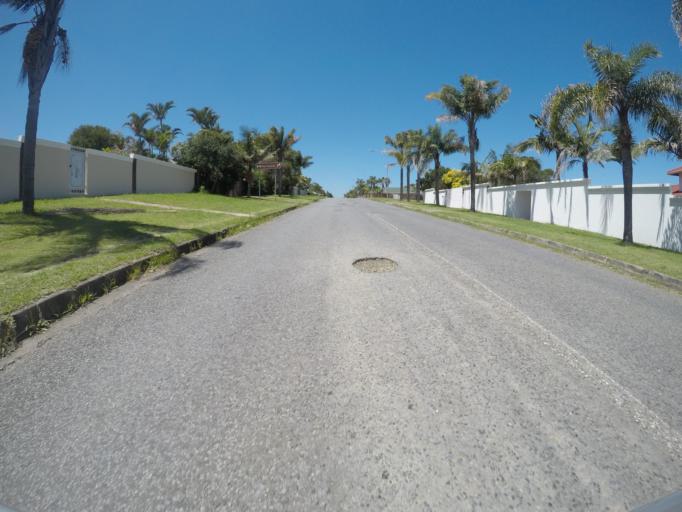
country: ZA
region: Eastern Cape
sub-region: Buffalo City Metropolitan Municipality
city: East London
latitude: -32.9589
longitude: 27.9372
